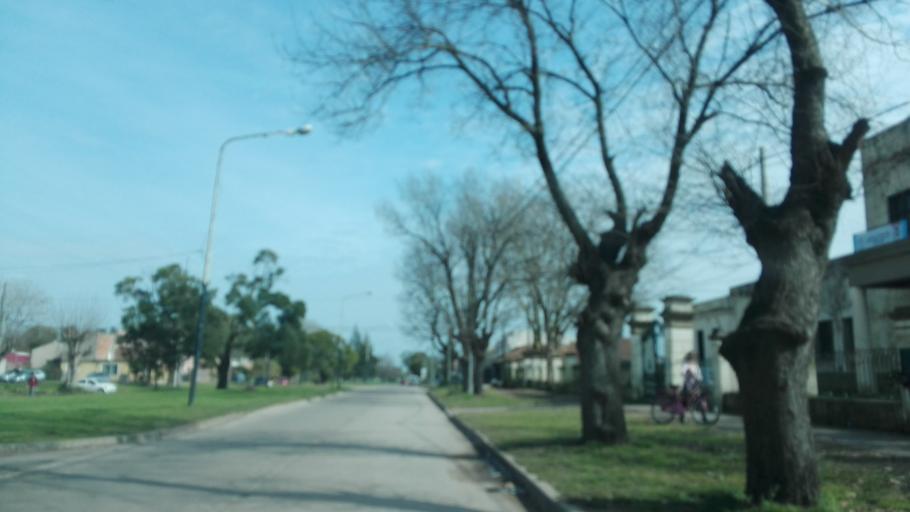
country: AR
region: Buenos Aires
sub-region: Partido de Chascomus
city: Chascomus
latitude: -35.5683
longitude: -58.0178
